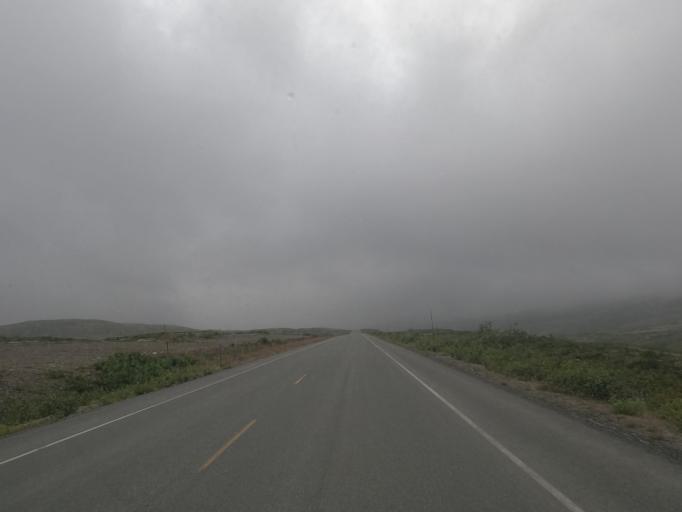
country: US
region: Alaska
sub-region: Haines Borough
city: Haines
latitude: 59.6839
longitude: -136.5776
